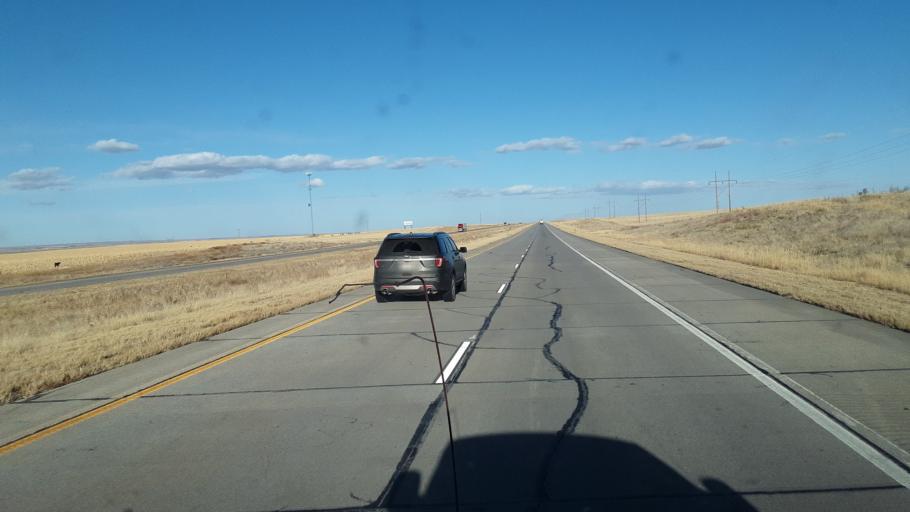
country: US
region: Colorado
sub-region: Logan County
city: Sterling
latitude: 40.7252
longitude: -103.0259
